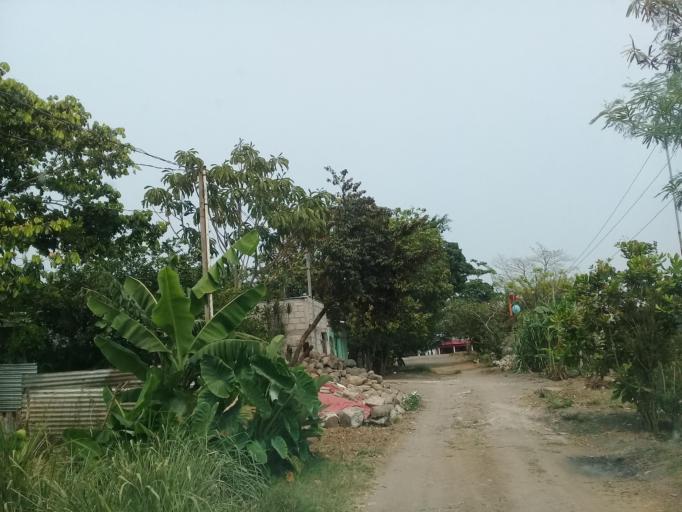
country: MX
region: Veracruz
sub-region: Medellin
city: La Laguna y Monte del Castillo
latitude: 18.9821
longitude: -96.1188
